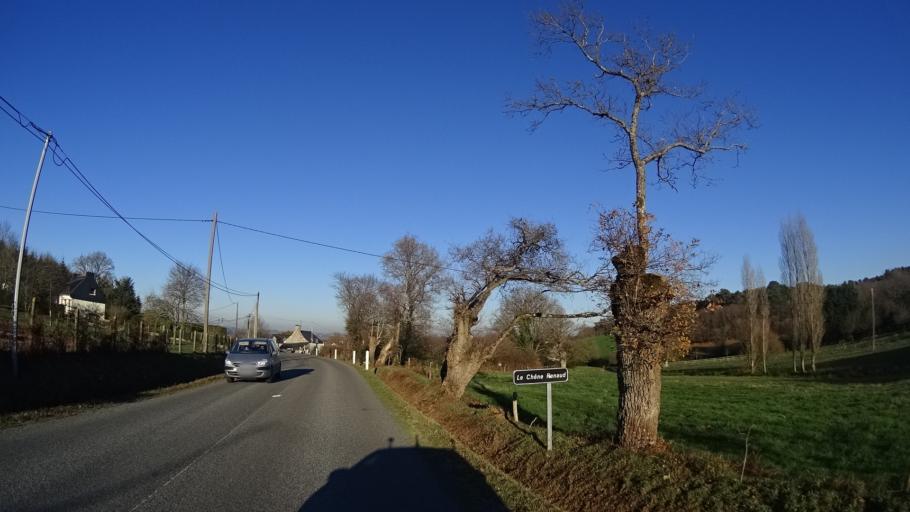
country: FR
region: Brittany
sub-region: Departement du Morbihan
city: Allaire
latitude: 47.6584
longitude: -2.1705
